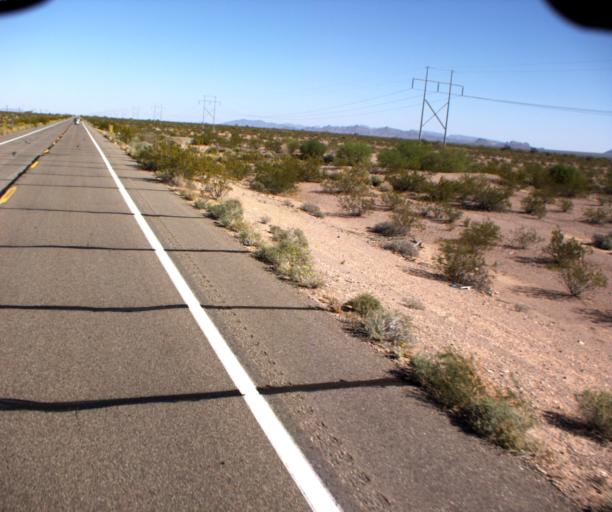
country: US
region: Arizona
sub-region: La Paz County
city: Quartzsite
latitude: 33.3281
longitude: -114.2169
